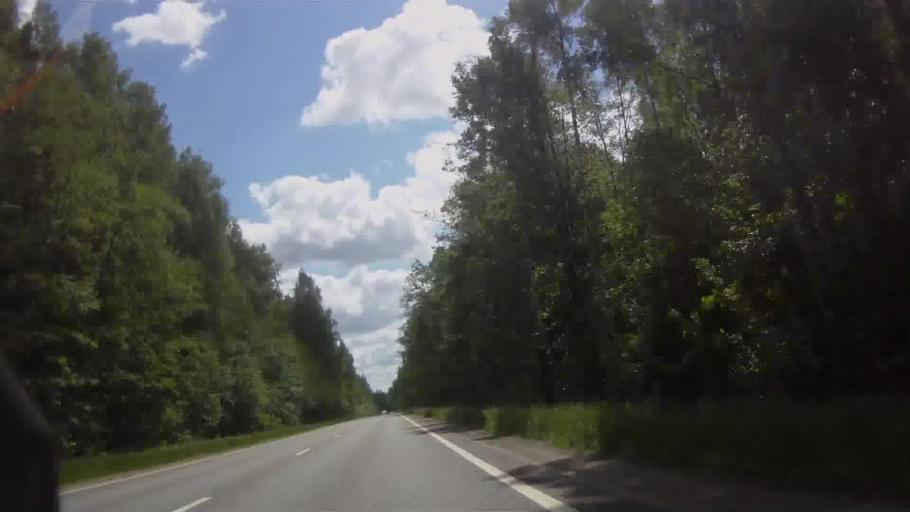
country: LV
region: Livani
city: Livani
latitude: 56.5261
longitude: 26.1558
